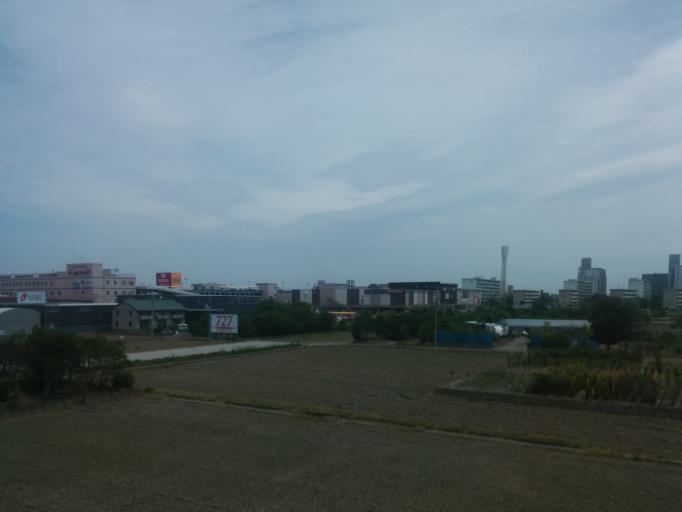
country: JP
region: Aichi
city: Inazawa
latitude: 35.2503
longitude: 136.7686
